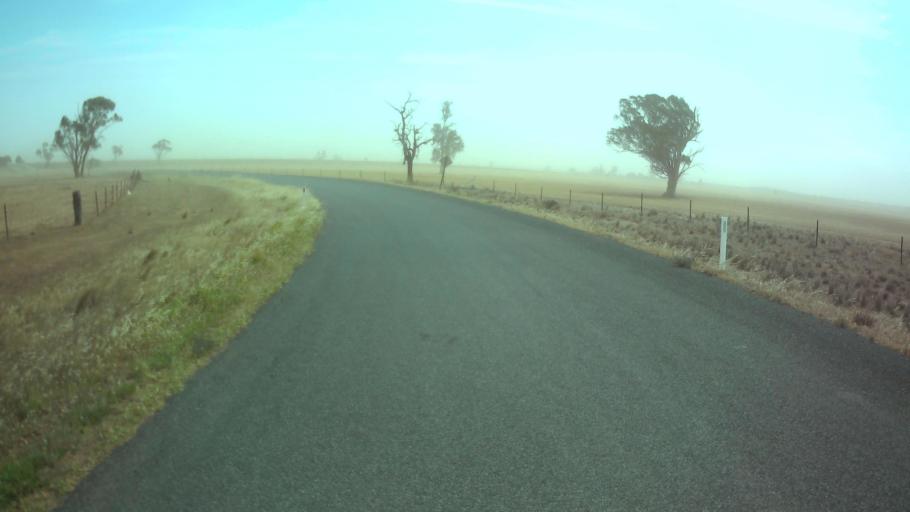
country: AU
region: New South Wales
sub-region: Weddin
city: Grenfell
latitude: -33.7360
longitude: 147.9969
